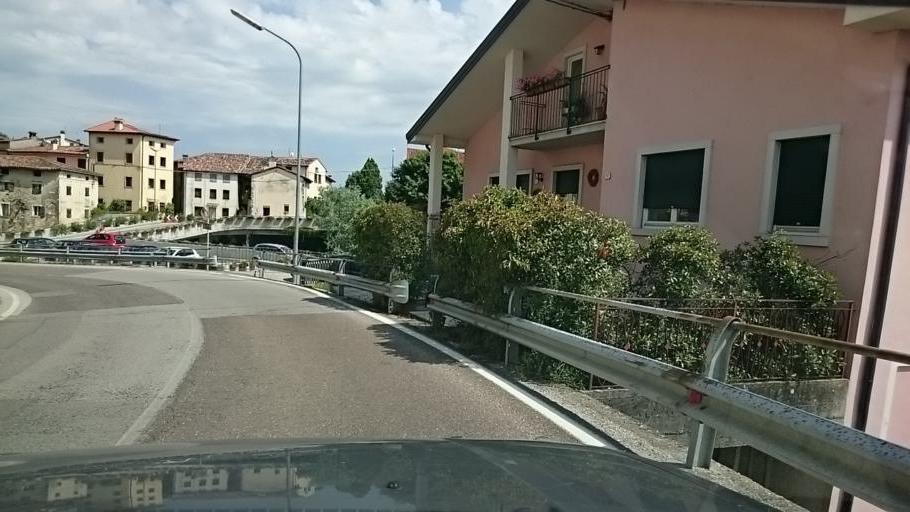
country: IT
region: Veneto
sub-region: Provincia di Vicenza
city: Conco
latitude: 45.7741
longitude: 11.6118
